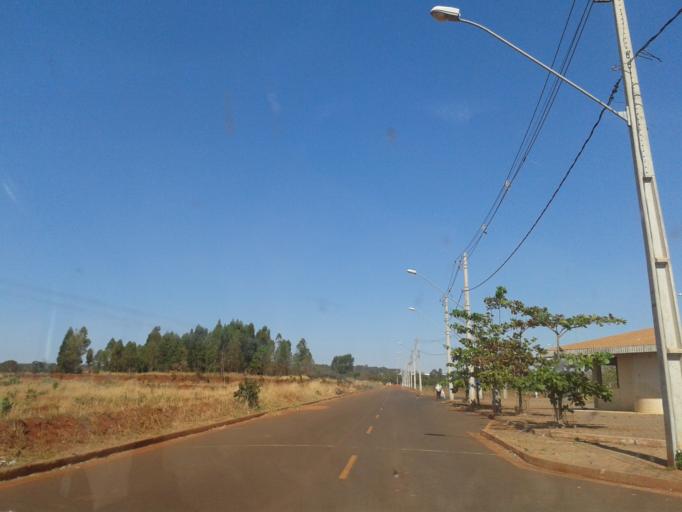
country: BR
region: Minas Gerais
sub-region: Ituiutaba
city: Ituiutaba
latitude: -19.0013
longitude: -49.4753
